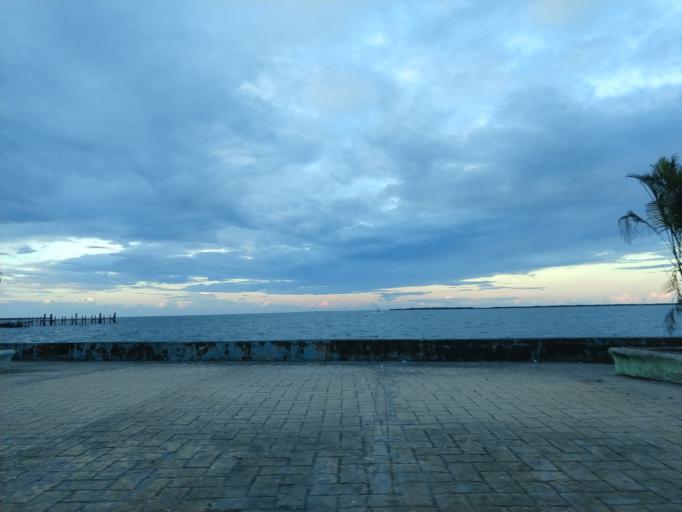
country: BZ
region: Belize
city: Belize City
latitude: 17.5032
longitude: -88.1878
